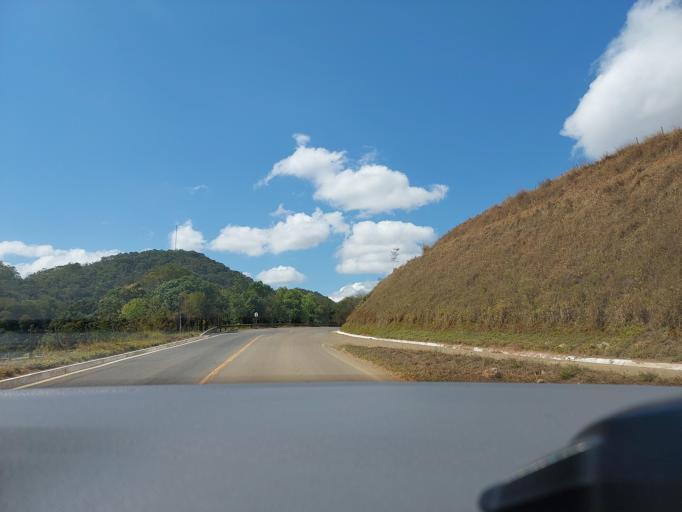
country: BR
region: Minas Gerais
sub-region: Muriae
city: Muriae
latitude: -21.0744
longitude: -42.5049
